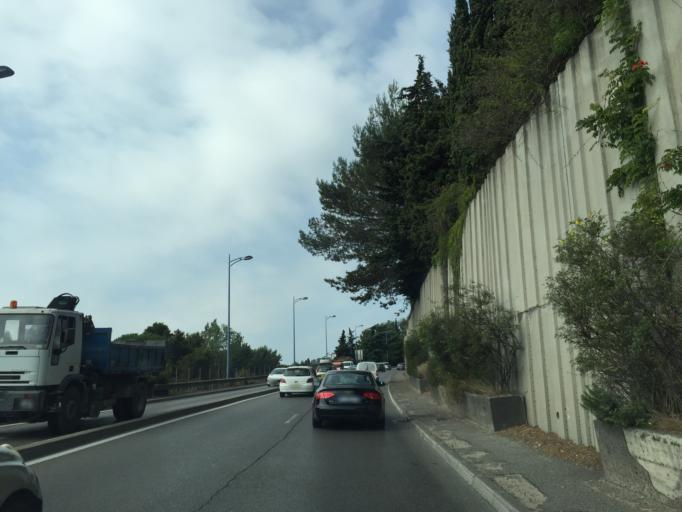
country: FR
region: Provence-Alpes-Cote d'Azur
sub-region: Departement des Alpes-Maritimes
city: Cagnes-sur-Mer
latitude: 43.6458
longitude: 7.1361
